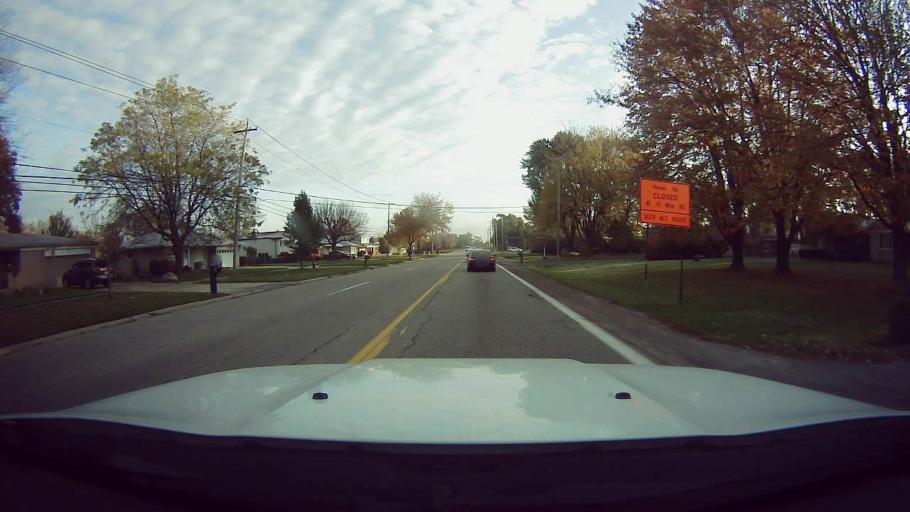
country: US
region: Michigan
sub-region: Macomb County
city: Fraser
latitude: 42.5558
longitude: -82.9738
